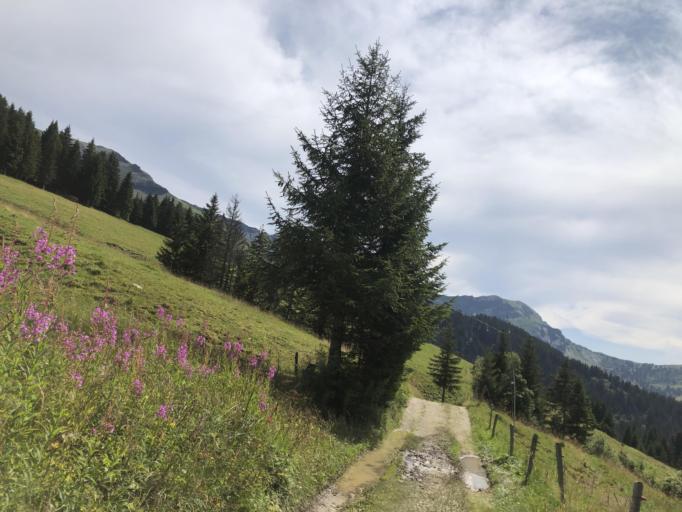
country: FR
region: Rhone-Alpes
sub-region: Departement de la Haute-Savoie
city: Megeve
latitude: 45.8346
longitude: 6.6688
